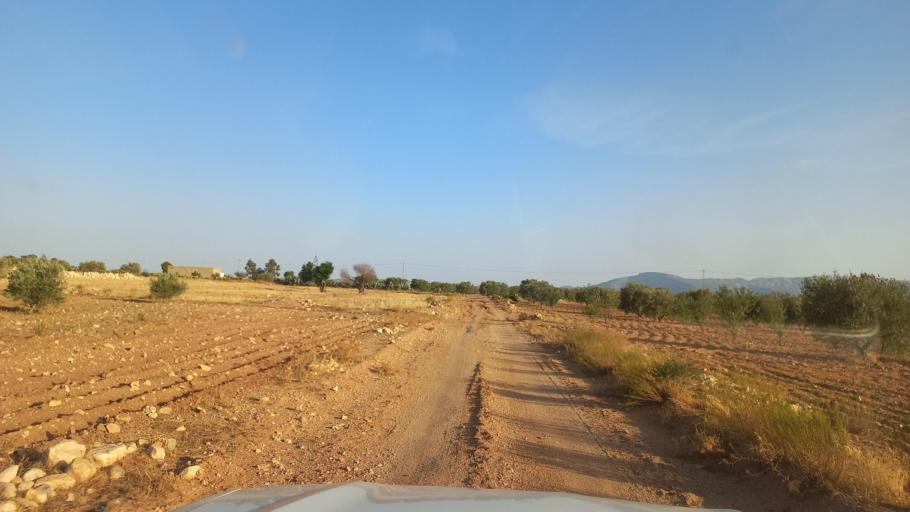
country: TN
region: Al Qasrayn
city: Kasserine
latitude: 35.2576
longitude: 8.9071
